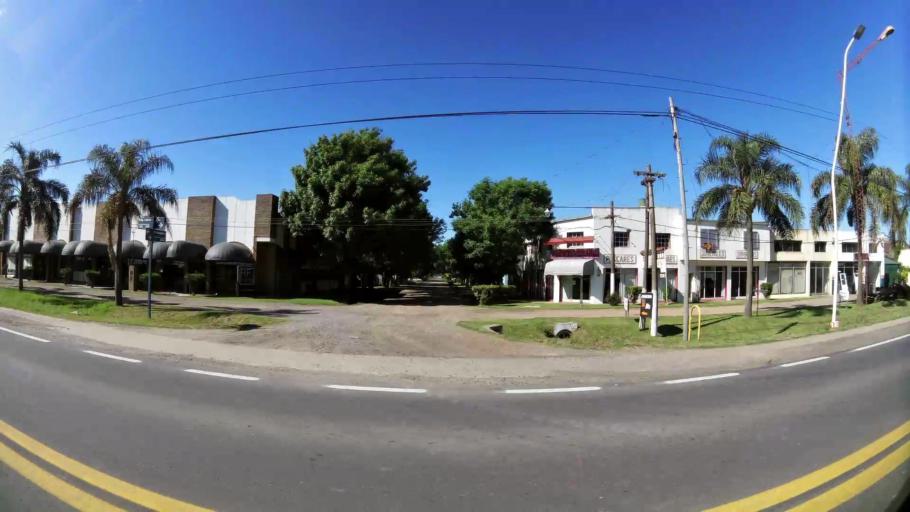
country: AR
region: Santa Fe
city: Esperanza
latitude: -31.4475
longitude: -60.9093
